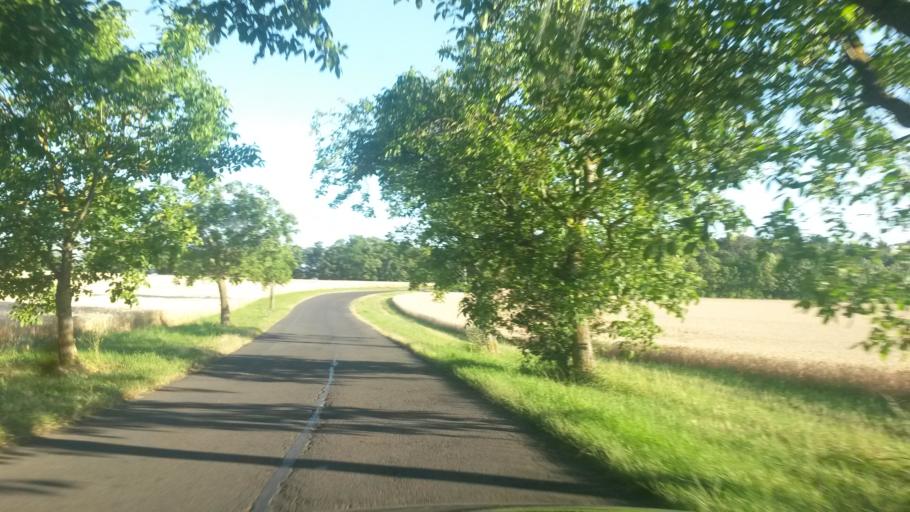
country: DE
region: Bavaria
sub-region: Regierungsbezirk Unterfranken
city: Wuerzburg
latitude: 49.8116
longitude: 9.9330
